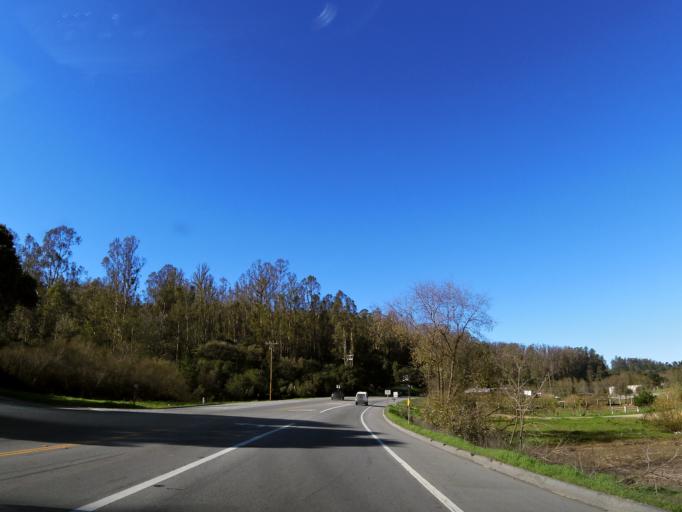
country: US
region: California
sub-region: Monterey County
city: Prunedale
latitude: 36.8082
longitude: -121.6716
